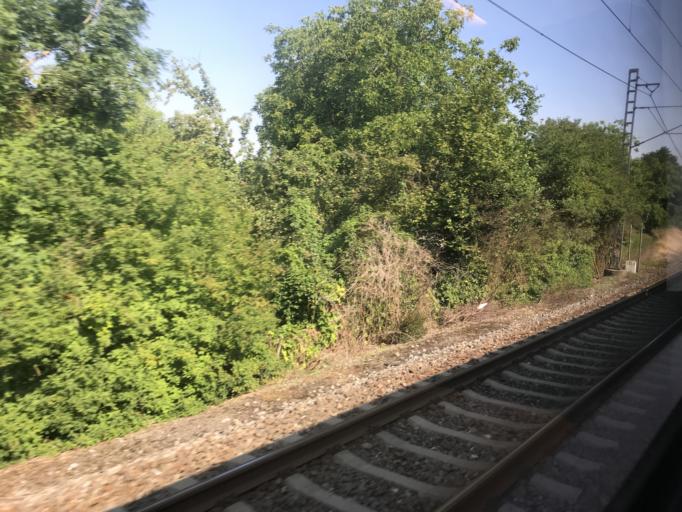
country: CZ
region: Central Bohemia
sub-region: Okres Praha-Vychod
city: Ricany
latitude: 49.9807
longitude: 14.6683
